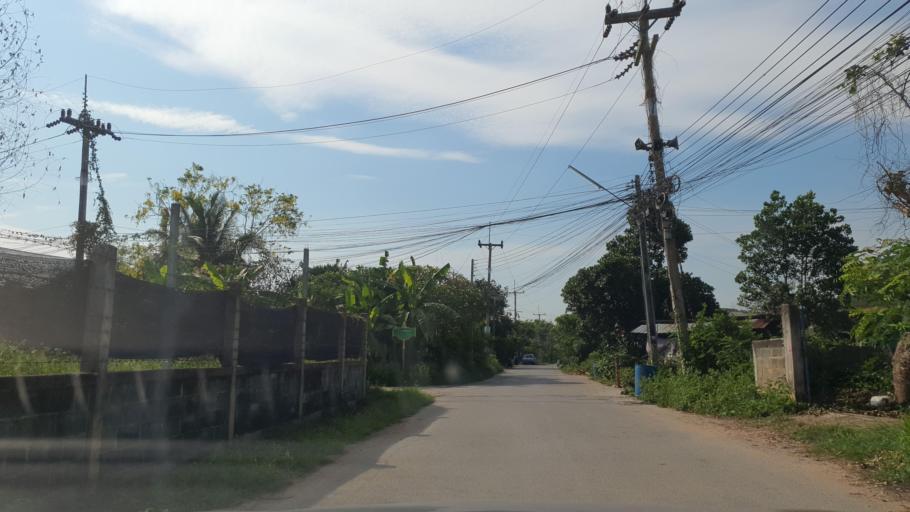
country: TH
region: Chon Buri
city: Sattahip
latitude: 12.7950
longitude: 100.9365
